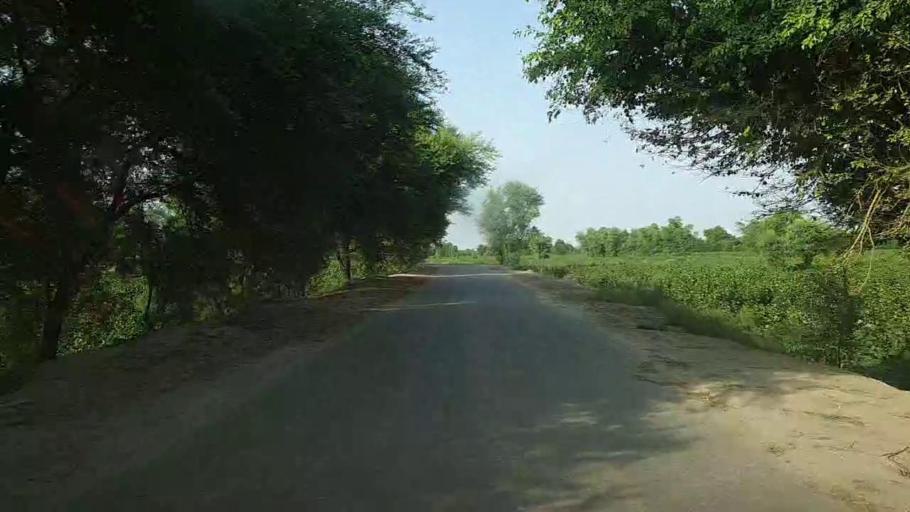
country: PK
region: Sindh
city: Ubauro
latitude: 28.1050
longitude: 69.8468
